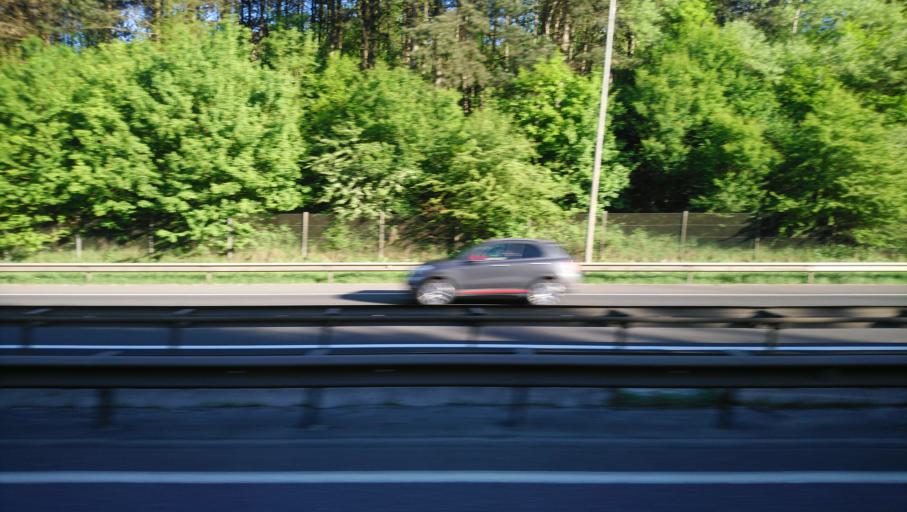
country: LU
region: Luxembourg
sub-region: Canton d'Esch-sur-Alzette
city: Leudelange
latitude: 49.5585
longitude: 6.0591
